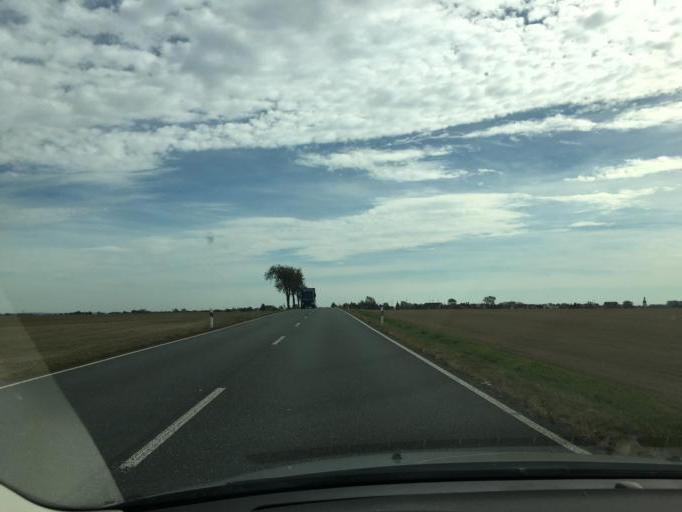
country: DE
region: Saxony
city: Riesa
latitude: 51.2564
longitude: 13.2765
